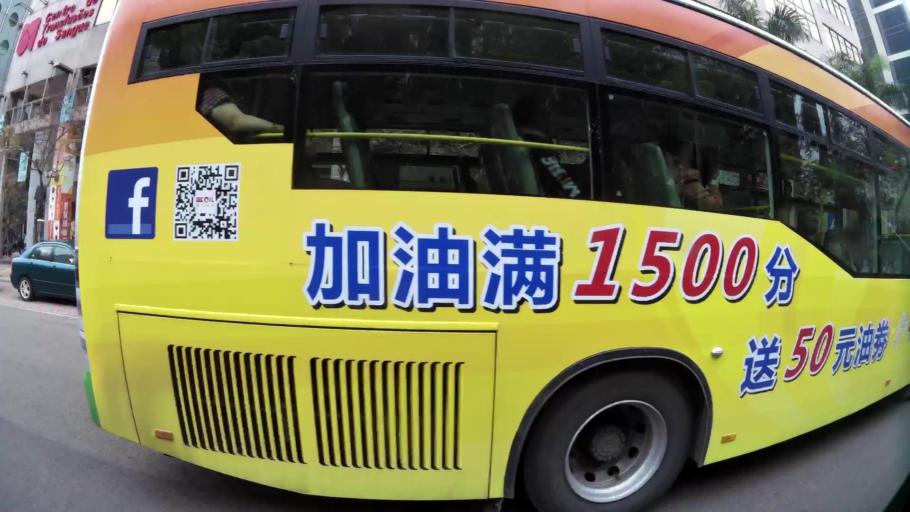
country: MO
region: Macau
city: Macau
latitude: 22.1891
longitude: 113.5507
